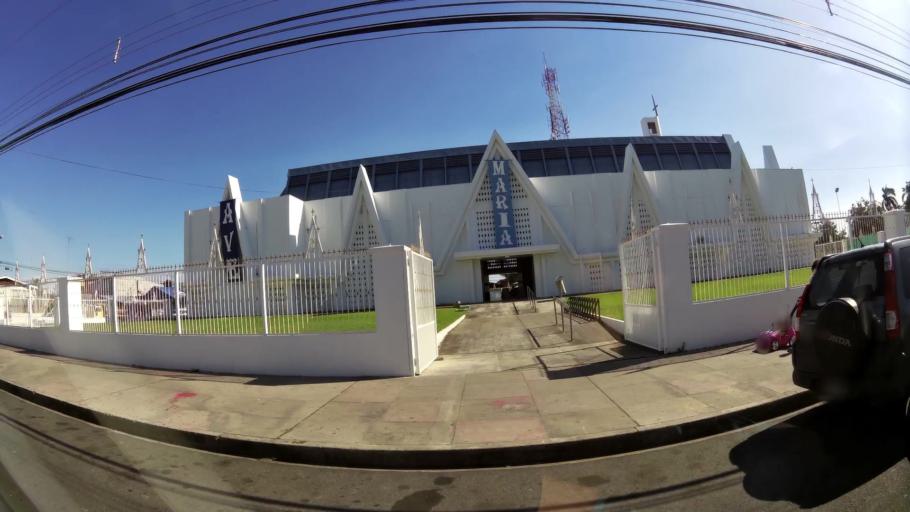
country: CR
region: Guanacaste
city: Liberia
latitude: 10.6304
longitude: -85.4376
